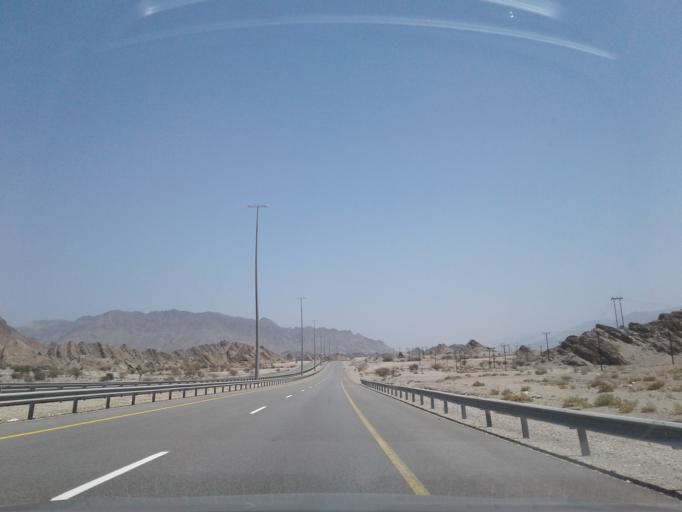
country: OM
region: Muhafazat Masqat
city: Muscat
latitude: 23.3491
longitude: 58.6906
